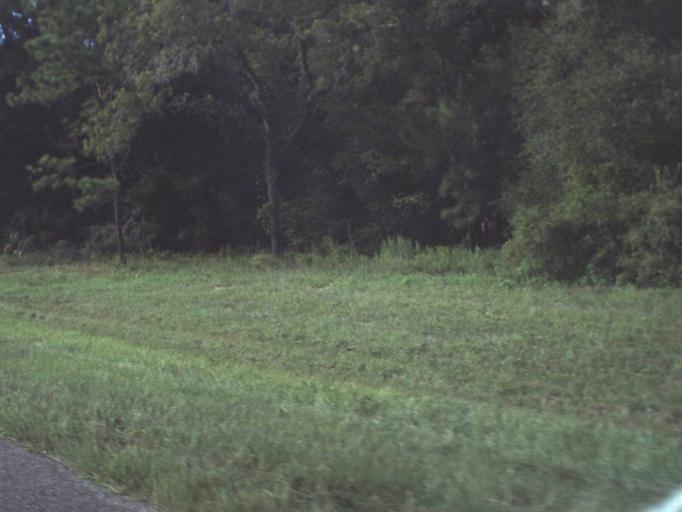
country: US
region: Florida
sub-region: Citrus County
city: Sugarmill Woods
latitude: 28.6722
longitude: -82.4787
